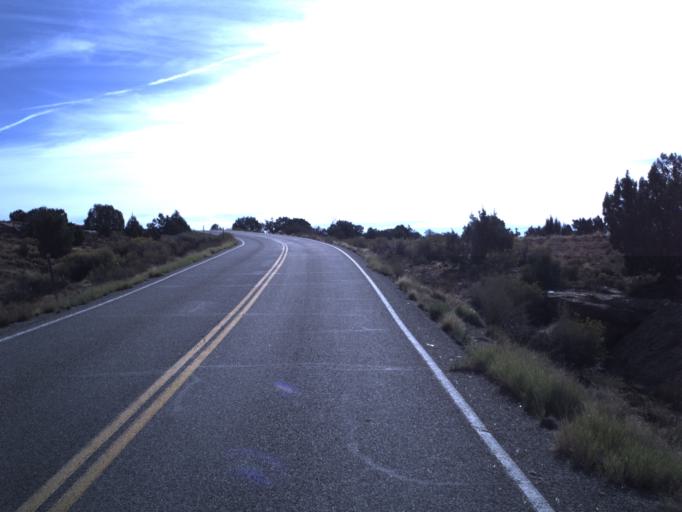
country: US
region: Utah
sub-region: San Juan County
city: Blanding
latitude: 37.4361
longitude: -109.3897
